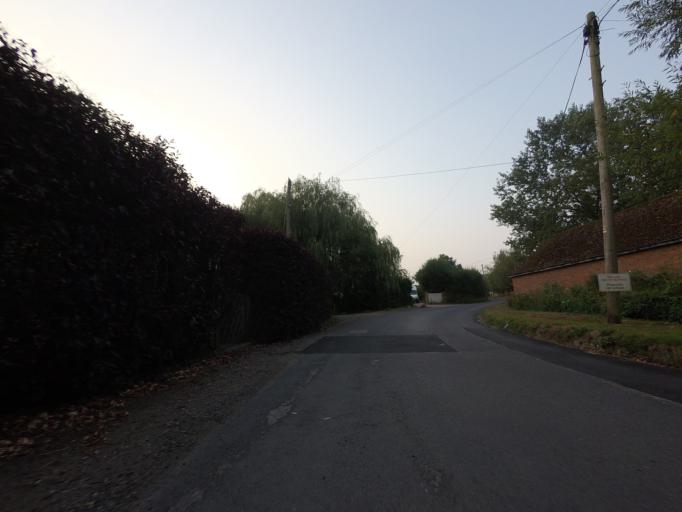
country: GB
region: England
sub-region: Kent
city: Headcorn
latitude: 51.1825
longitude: 0.6693
